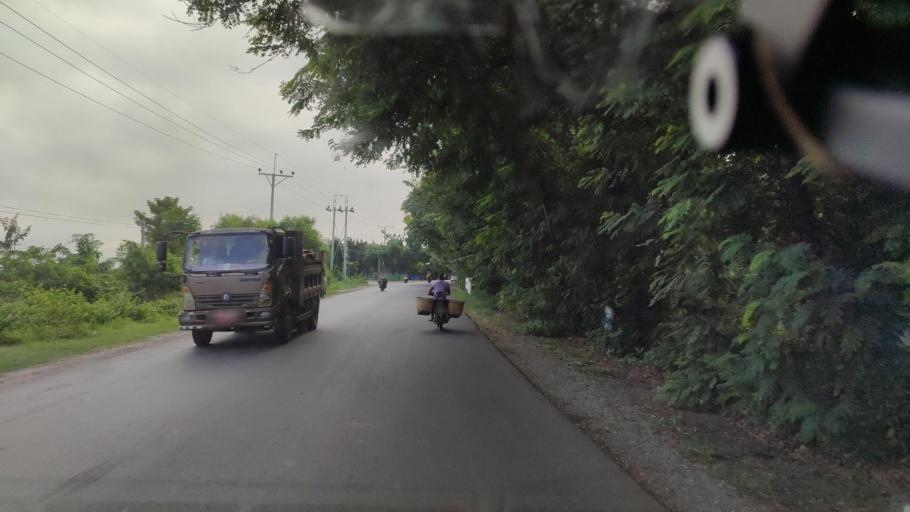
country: MM
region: Mandalay
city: Mandalay
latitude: 22.1111
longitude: 96.1530
